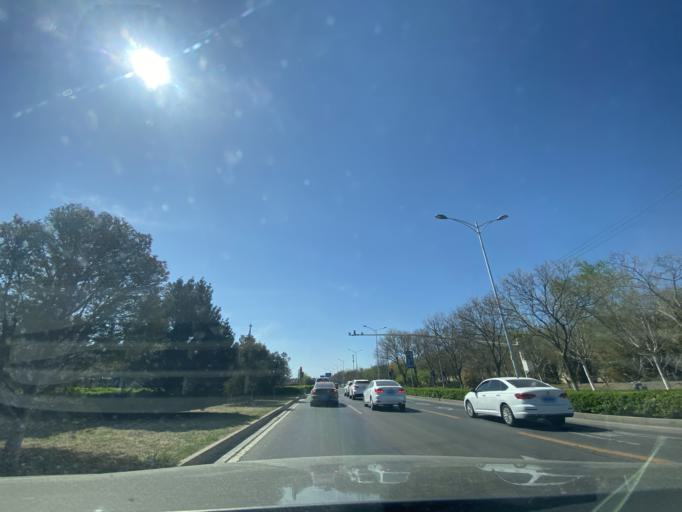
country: CN
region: Beijing
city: Sijiqing
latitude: 39.9427
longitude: 116.2406
